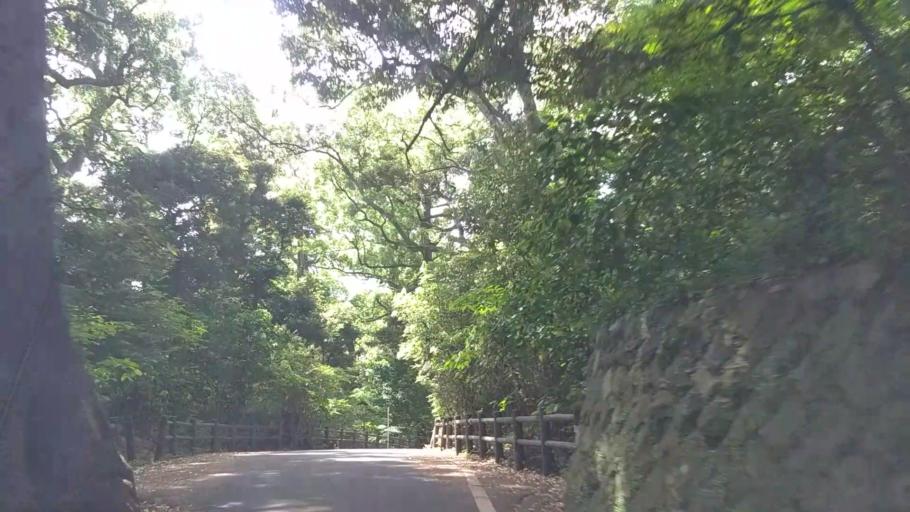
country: JP
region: Kanagawa
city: Yugawara
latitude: 35.1459
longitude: 139.1575
